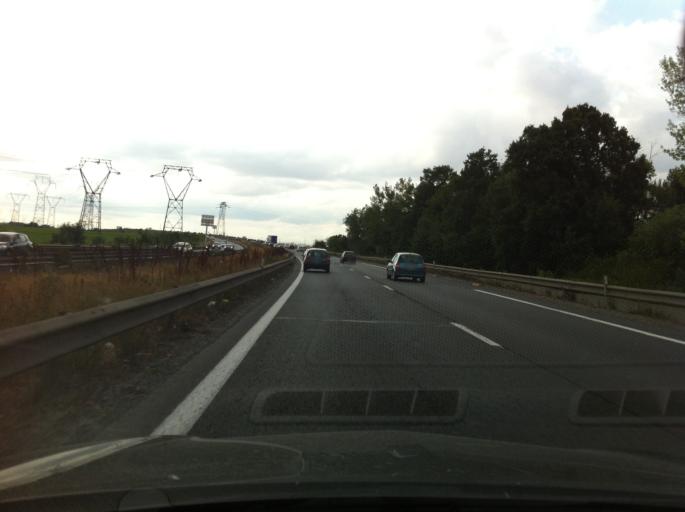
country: FR
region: Ile-de-France
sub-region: Departement de Seine-et-Marne
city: Villeparisis
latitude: 48.9555
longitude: 2.6268
